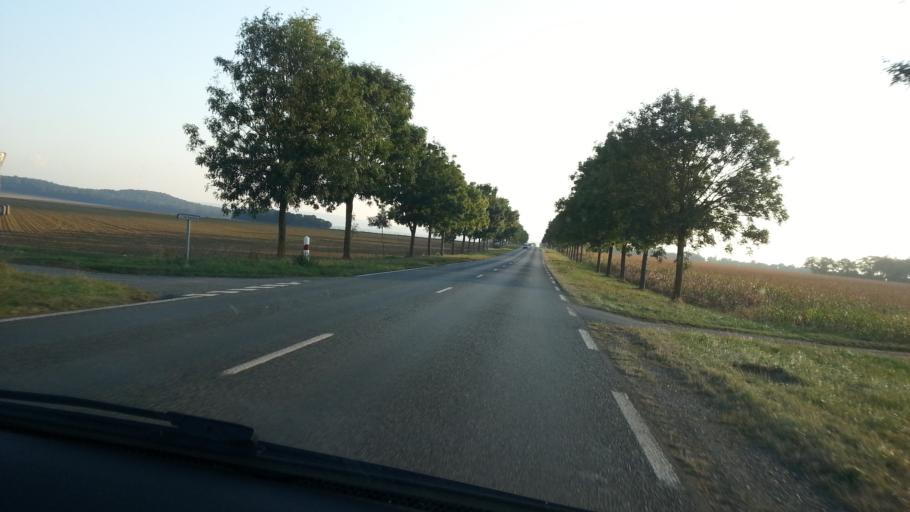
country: FR
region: Picardie
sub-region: Departement de l'Oise
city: Estrees-Saint-Denis
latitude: 49.3977
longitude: 2.6245
